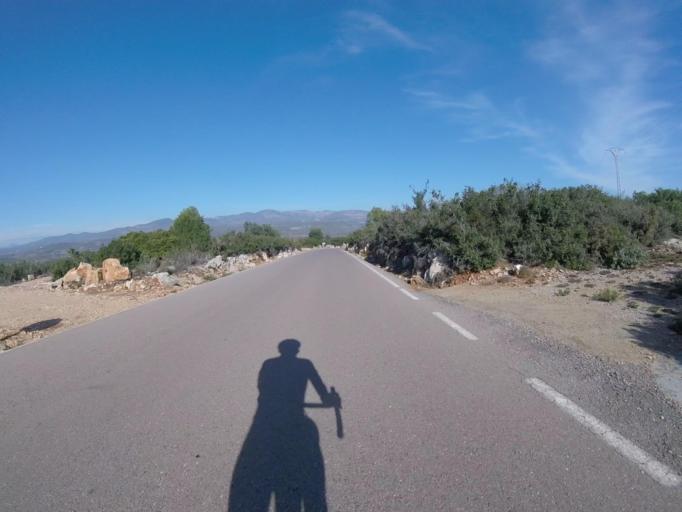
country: ES
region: Valencia
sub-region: Provincia de Castello
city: Benlloch
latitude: 40.2388
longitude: 0.0718
